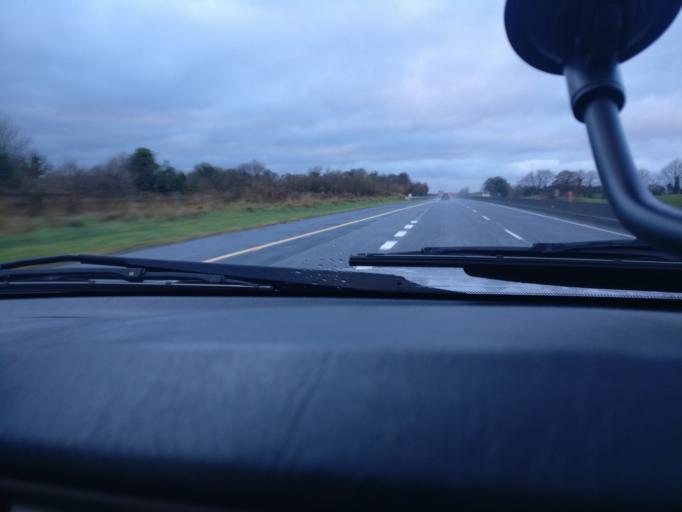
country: IE
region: Leinster
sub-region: An Iarmhi
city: Athlone
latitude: 53.4005
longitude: -7.8386
